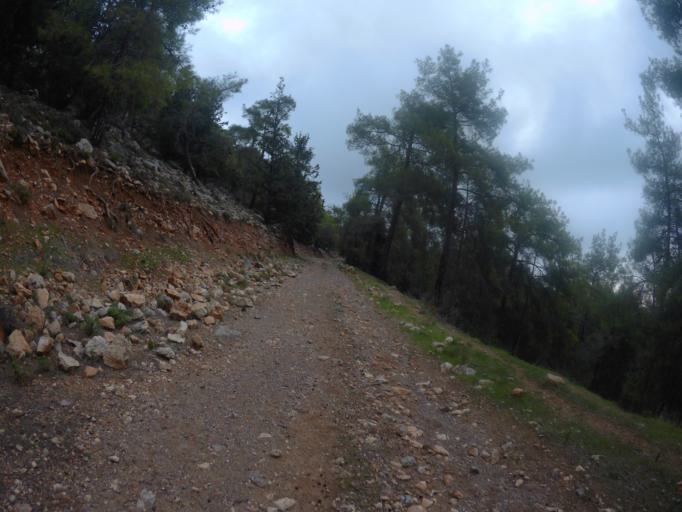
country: CY
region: Ammochostos
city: Lefkonoiko
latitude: 35.3018
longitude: 33.5747
